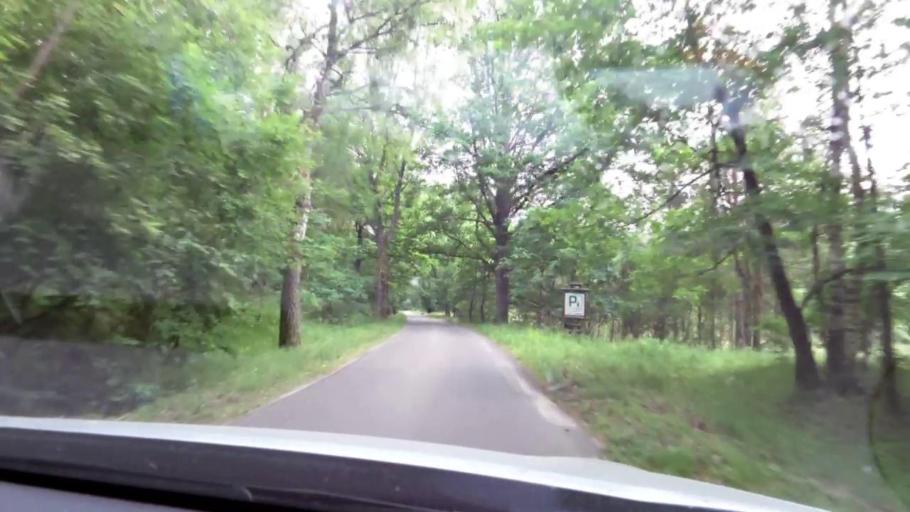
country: PL
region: Pomeranian Voivodeship
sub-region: Powiat bytowski
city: Trzebielino
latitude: 54.2431
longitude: 17.0000
